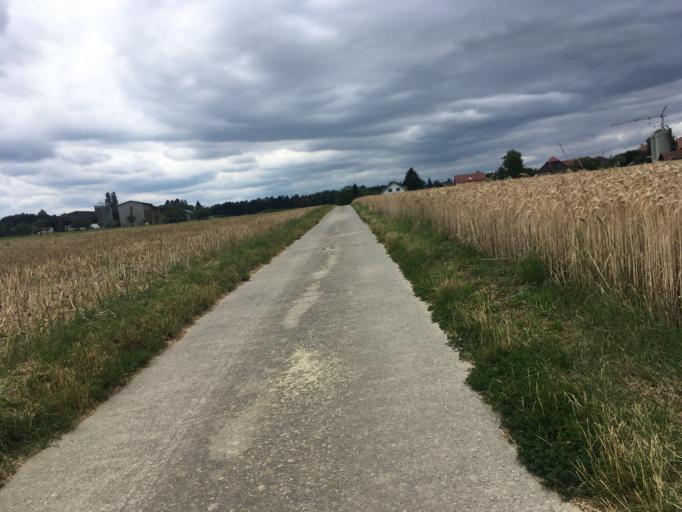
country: CH
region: Vaud
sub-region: Broye-Vully District
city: Payerne
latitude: 46.8732
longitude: 6.9091
